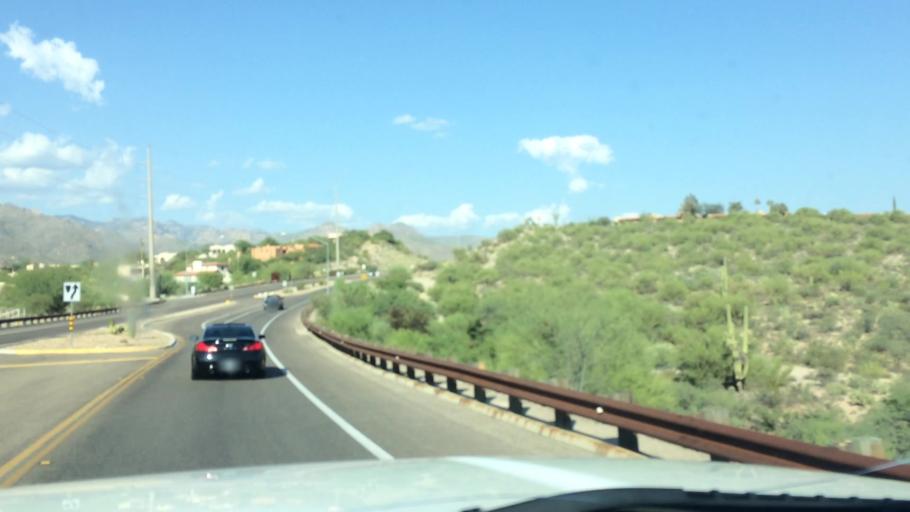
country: US
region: Arizona
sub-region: Pima County
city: Catalina Foothills
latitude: 32.3080
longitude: -110.8612
